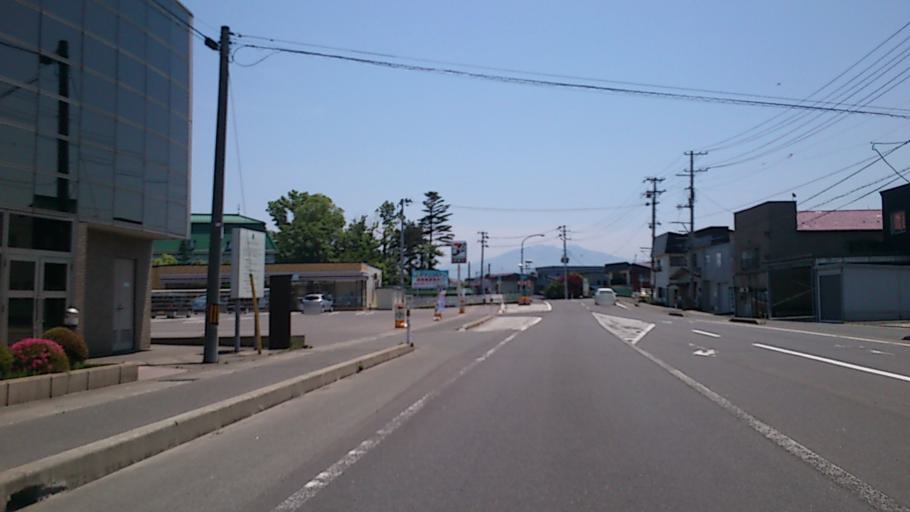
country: JP
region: Aomori
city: Aomori Shi
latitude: 40.8325
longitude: 140.7240
